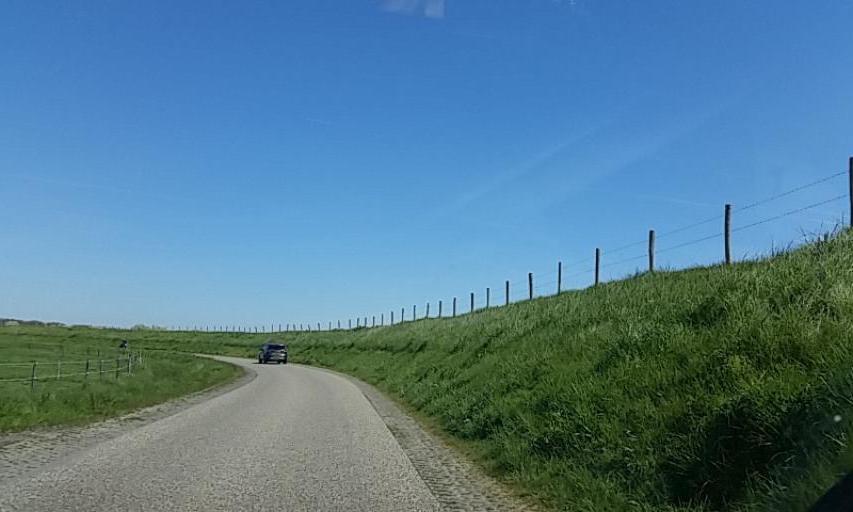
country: NL
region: Zeeland
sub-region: Gemeente Borsele
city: Borssele
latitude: 51.3245
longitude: 3.7191
